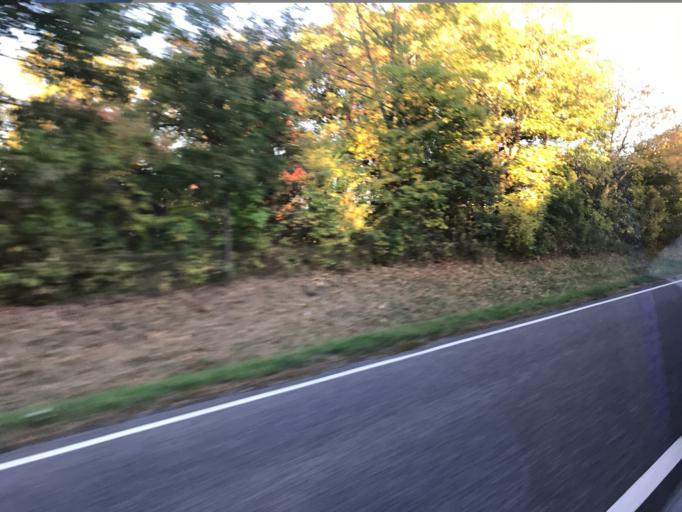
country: DE
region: Hesse
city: Kelkheim (Taunus)
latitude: 50.1410
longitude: 8.4610
